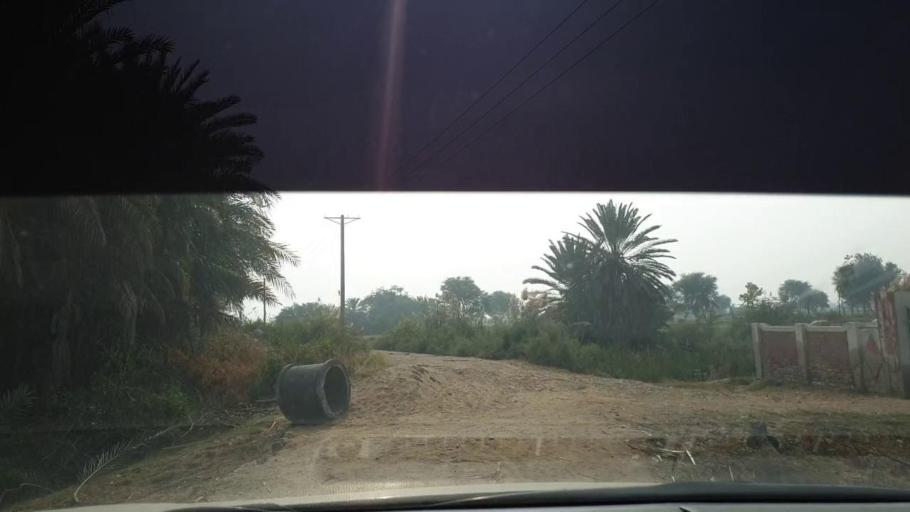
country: PK
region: Sindh
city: Berani
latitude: 25.8464
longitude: 68.8447
